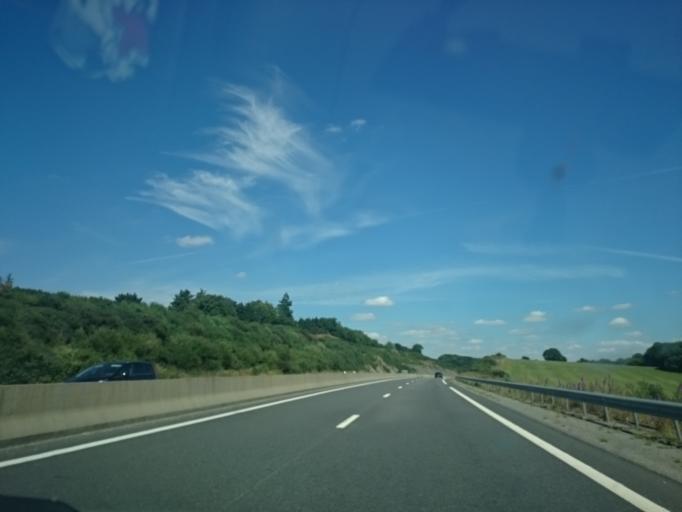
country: FR
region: Brittany
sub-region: Departement du Morbihan
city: Cleguerec
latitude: 48.2214
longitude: -3.0795
